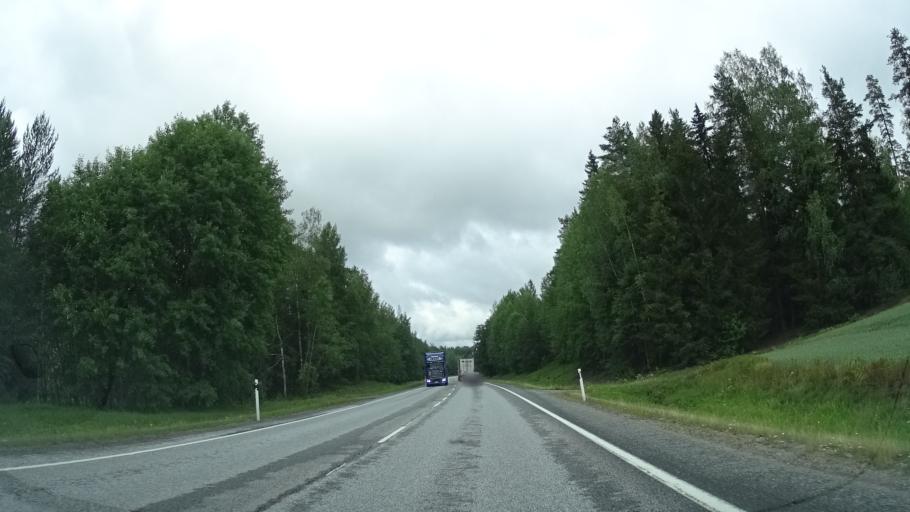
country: FI
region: Uusimaa
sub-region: Helsinki
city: Vihti
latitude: 60.4520
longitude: 24.3226
